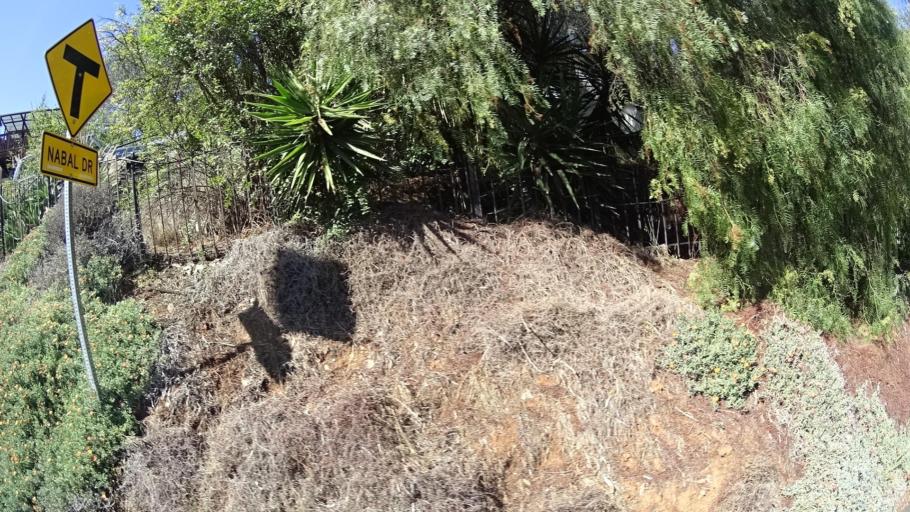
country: US
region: California
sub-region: San Diego County
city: Casa de Oro-Mount Helix
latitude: 32.7601
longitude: -116.9639
